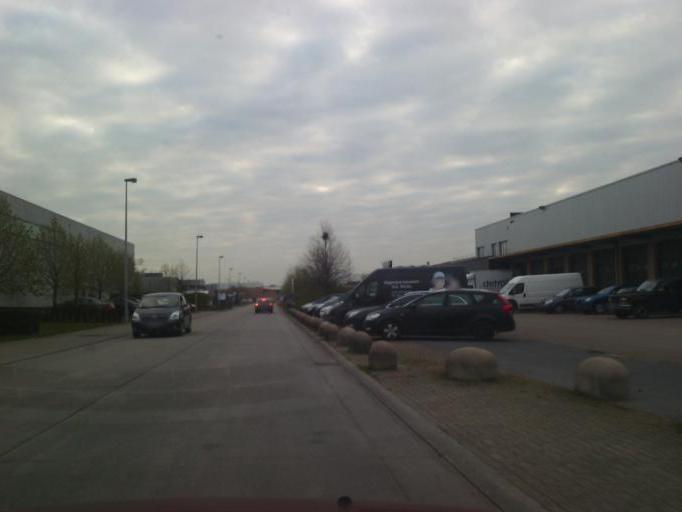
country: BE
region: Flanders
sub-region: Provincie Oost-Vlaanderen
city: Lokeren
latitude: 51.0836
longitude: 4.0026
